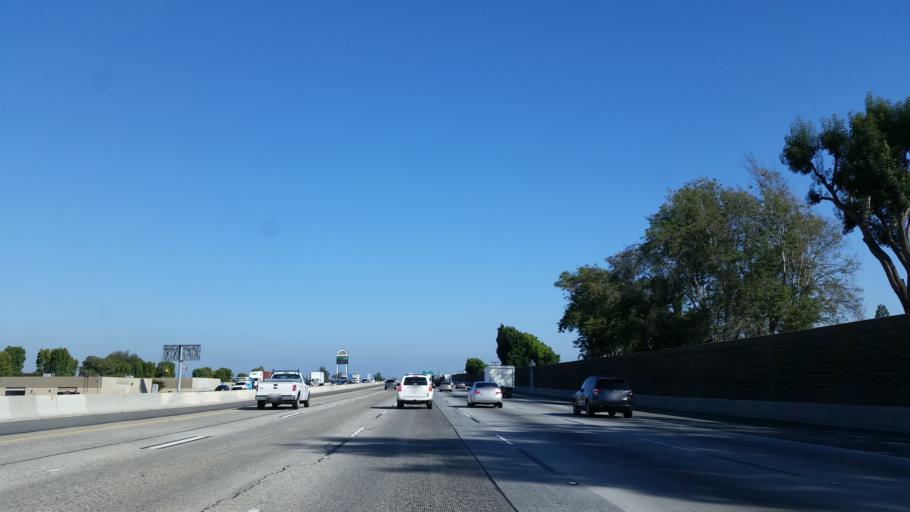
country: US
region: California
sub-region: Orange County
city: Garden Grove
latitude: 33.7658
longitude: -117.9478
